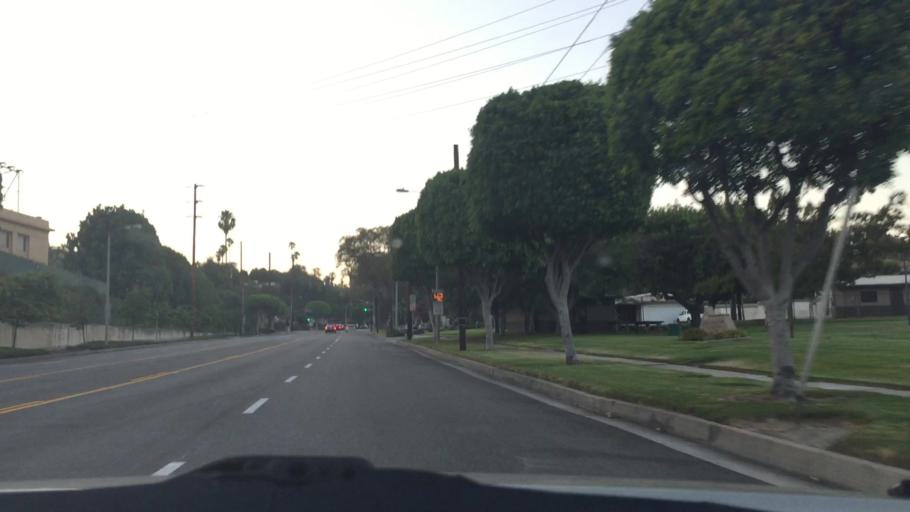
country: US
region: California
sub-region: Los Angeles County
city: Monterey Park
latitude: 34.0449
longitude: -118.1284
